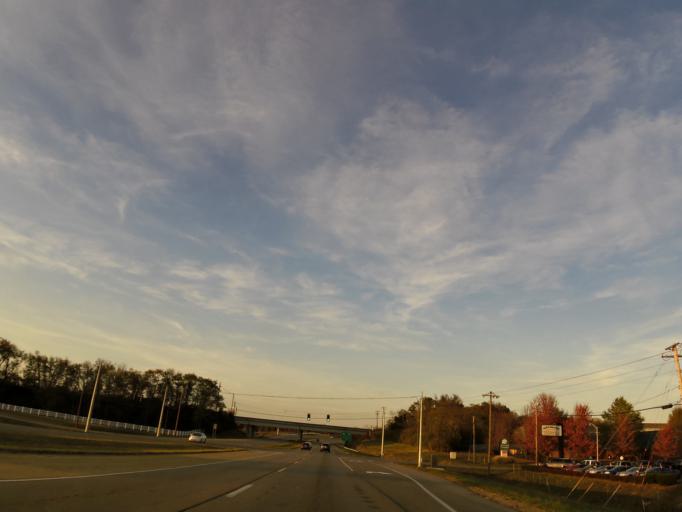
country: US
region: Kentucky
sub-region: Jessamine County
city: Nicholasville
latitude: 37.8765
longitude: -84.5972
